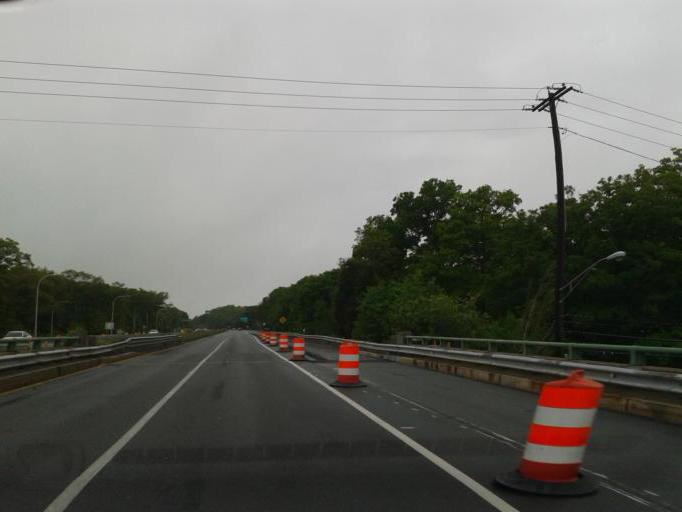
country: US
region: Rhode Island
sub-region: Newport County
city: Tiverton
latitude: 41.6414
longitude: -71.1872
